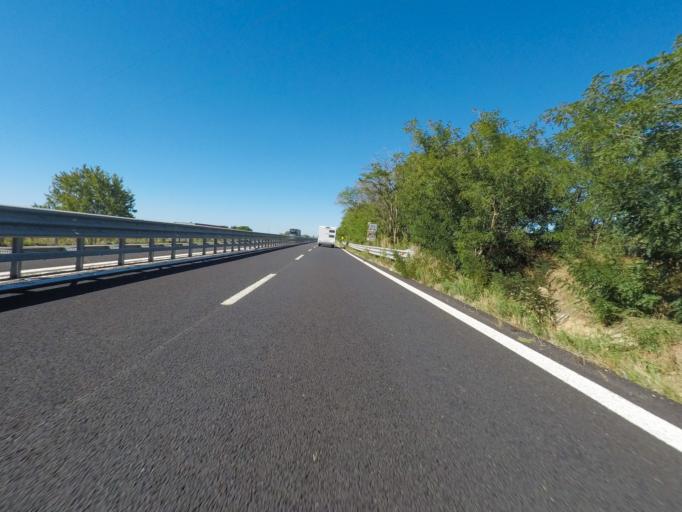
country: IT
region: Latium
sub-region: Provincia di Viterbo
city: Tarquinia
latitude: 42.2710
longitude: 11.7139
